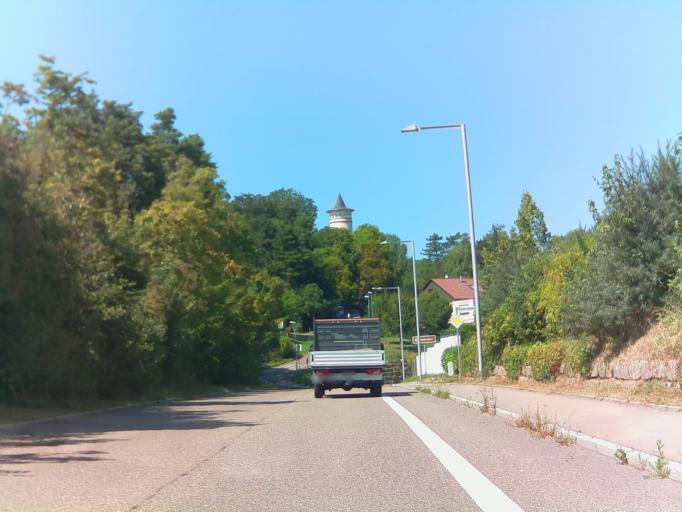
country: DE
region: Baden-Wuerttemberg
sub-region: Regierungsbezirk Stuttgart
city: Leonberg
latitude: 48.7995
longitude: 9.0278
